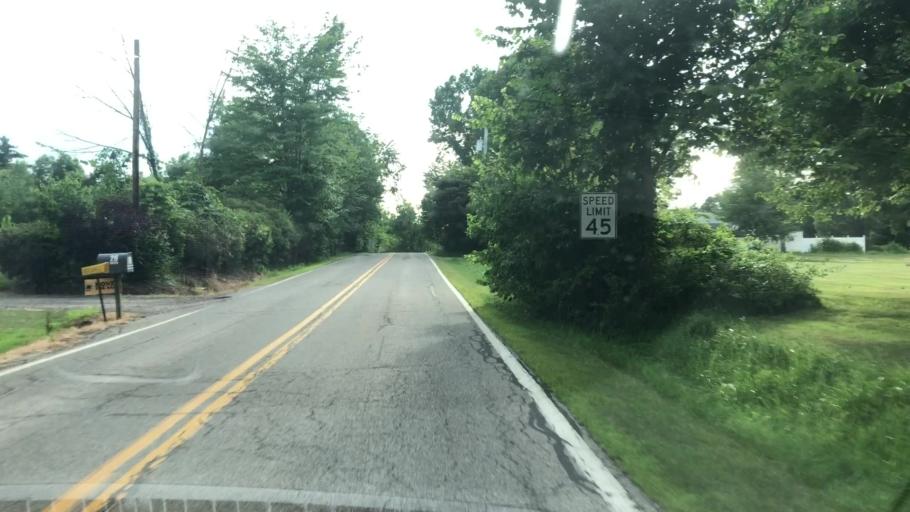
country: US
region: Ohio
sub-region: Summit County
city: Montrose-Ghent
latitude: 41.0994
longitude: -81.6877
